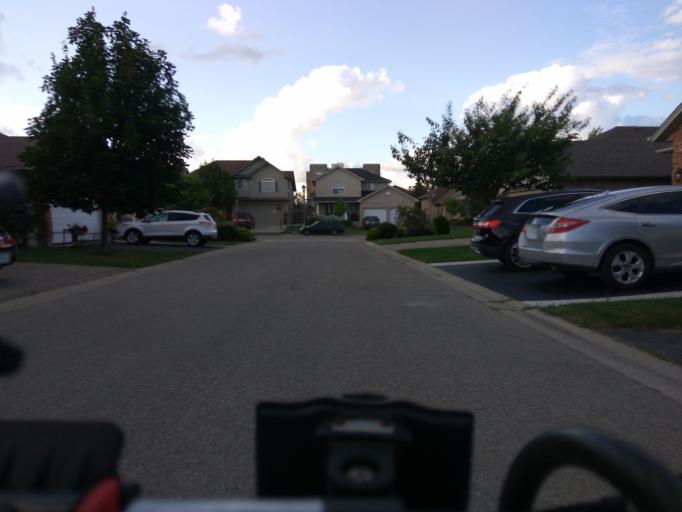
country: CA
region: Ontario
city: Stratford
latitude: 43.3811
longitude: -80.9625
